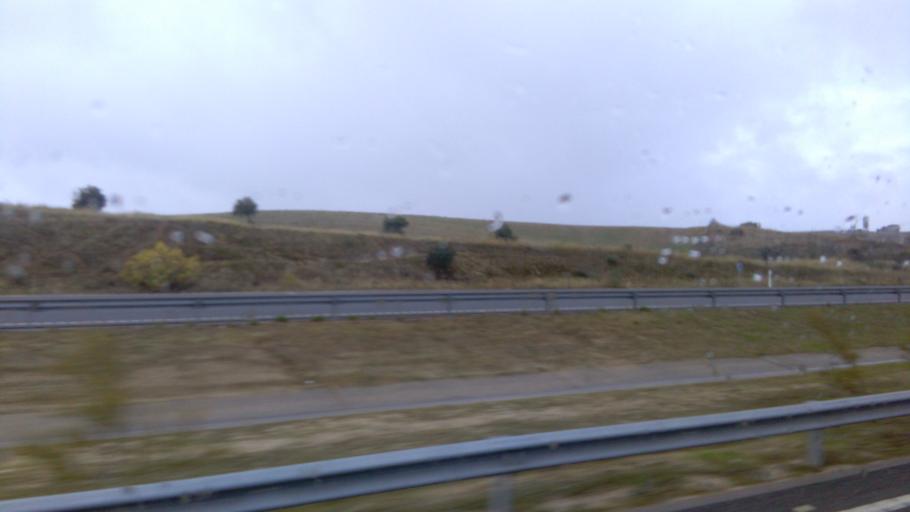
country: ES
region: Madrid
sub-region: Provincia de Madrid
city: Arroyomolinos
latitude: 40.2587
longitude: -3.9400
